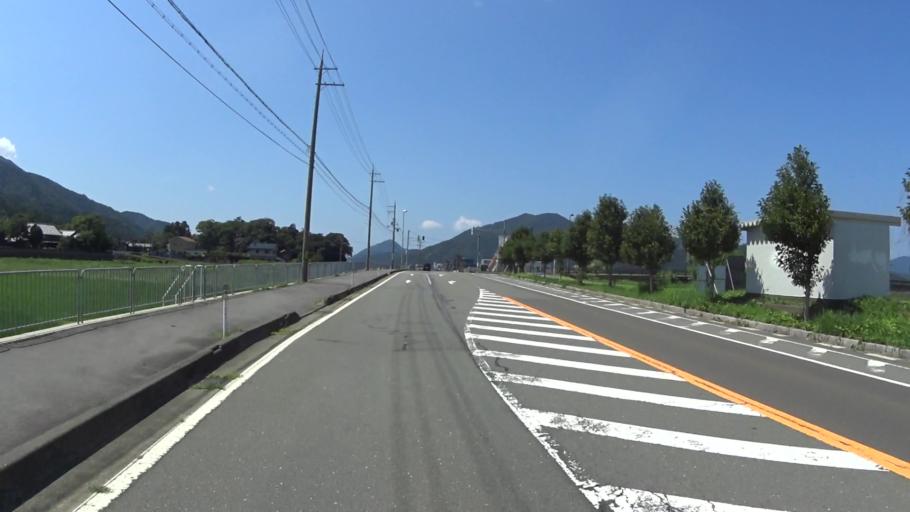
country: JP
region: Fukui
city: Obama
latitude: 35.4581
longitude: 135.8696
